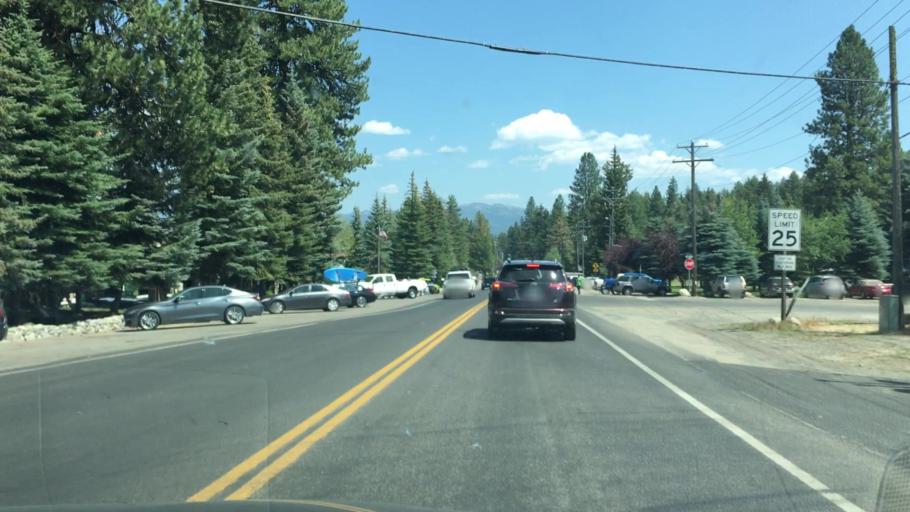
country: US
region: Idaho
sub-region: Valley County
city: McCall
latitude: 44.9125
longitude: -116.1218
